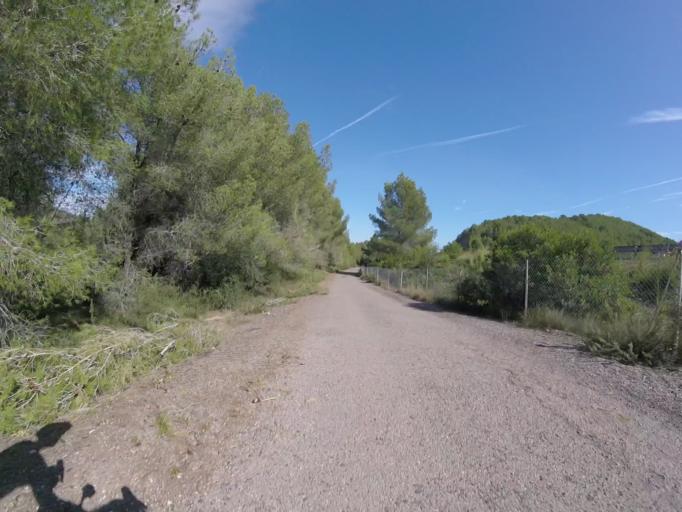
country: ES
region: Valencia
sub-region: Provincia de Castello
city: Santa Magdalena de Pulpis
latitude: 40.3880
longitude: 0.3472
